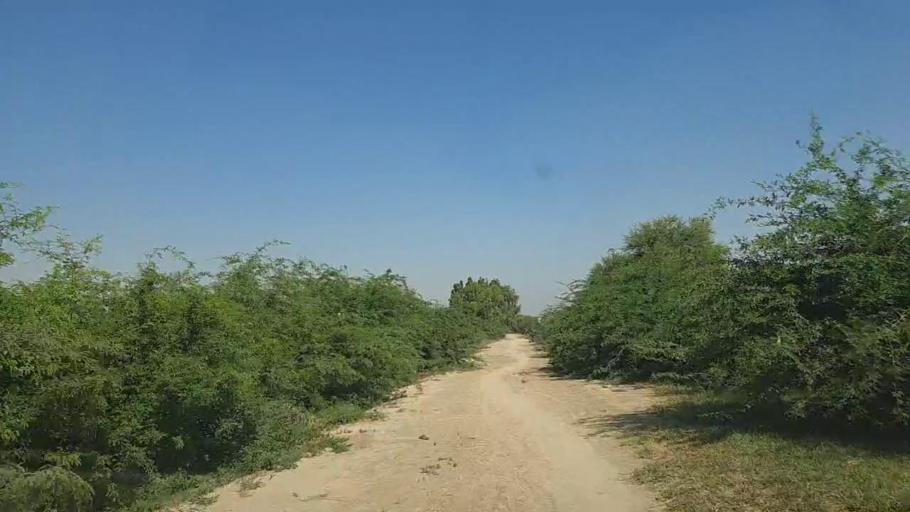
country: PK
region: Sindh
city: Thatta
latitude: 24.7937
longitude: 67.9777
